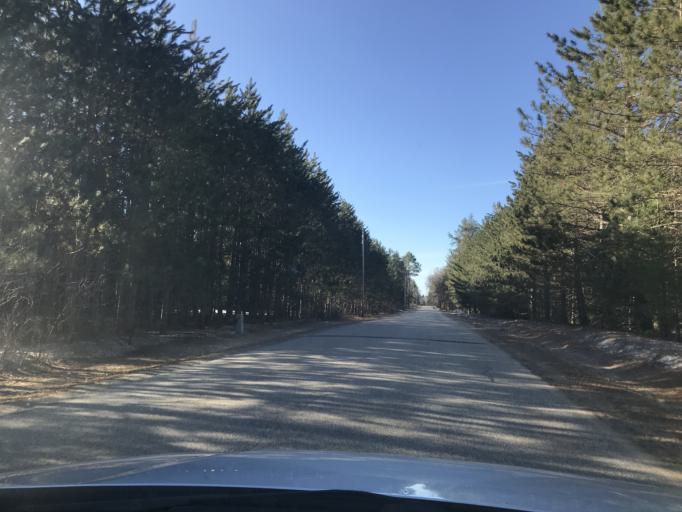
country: US
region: Michigan
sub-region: Dickinson County
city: Kingsford
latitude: 45.3950
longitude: -88.1612
